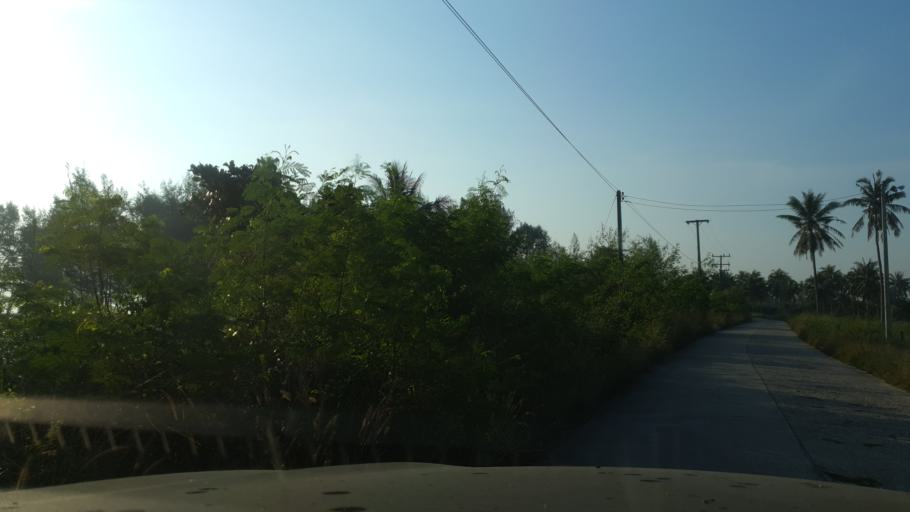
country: TH
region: Prachuap Khiri Khan
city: Bang Saphan
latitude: 11.2836
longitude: 99.5491
